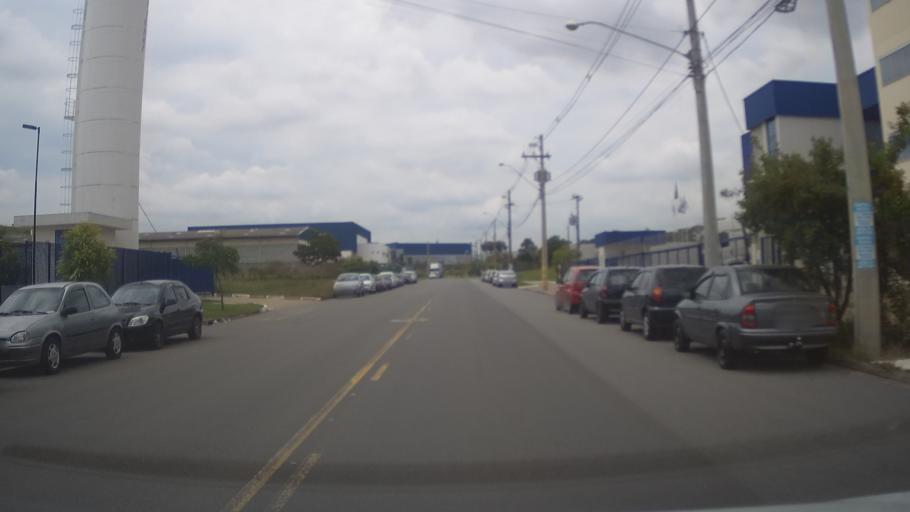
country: BR
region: Sao Paulo
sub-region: Itupeva
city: Itupeva
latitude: -23.1499
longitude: -47.0221
